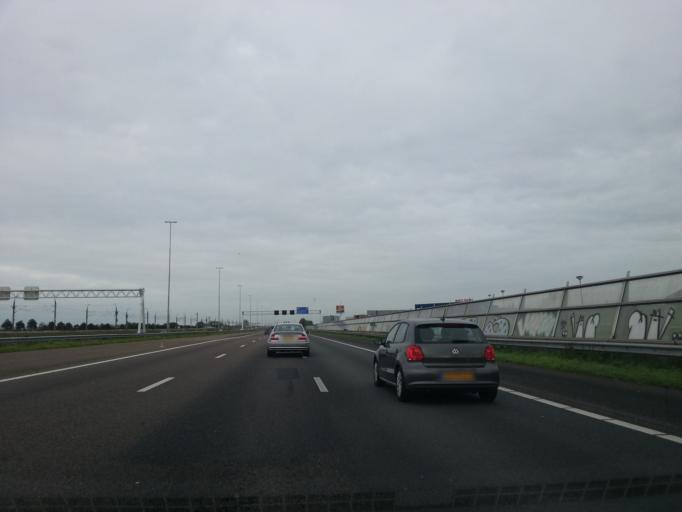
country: NL
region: South Holland
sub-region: Gemeente Kaag en Braassem
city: Oude Wetering
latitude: 52.1915
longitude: 4.6071
